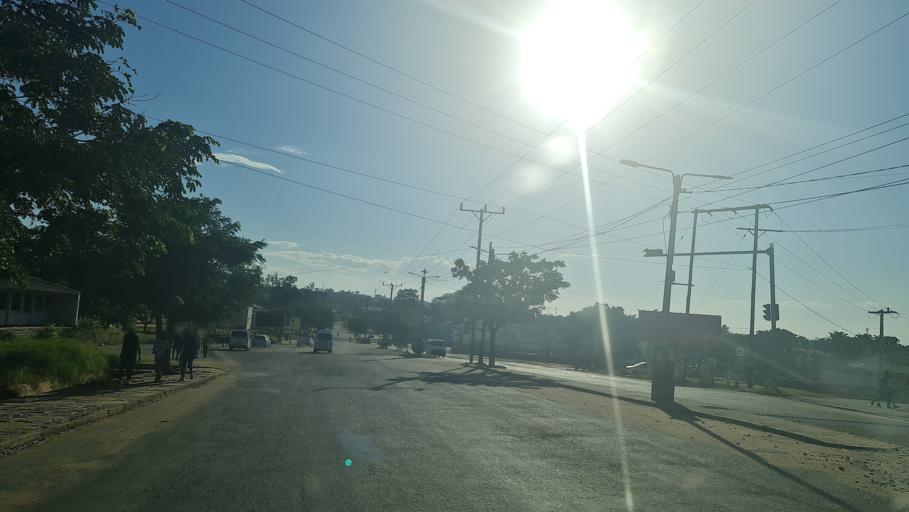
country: MZ
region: Cabo Delgado
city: Pemba
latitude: -12.9679
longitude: 40.5127
